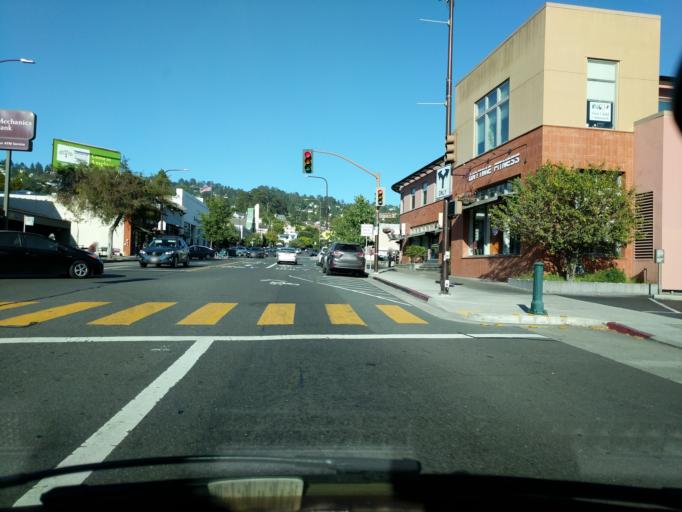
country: US
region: California
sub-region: Alameda County
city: Albany
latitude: 37.8913
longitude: -122.2800
